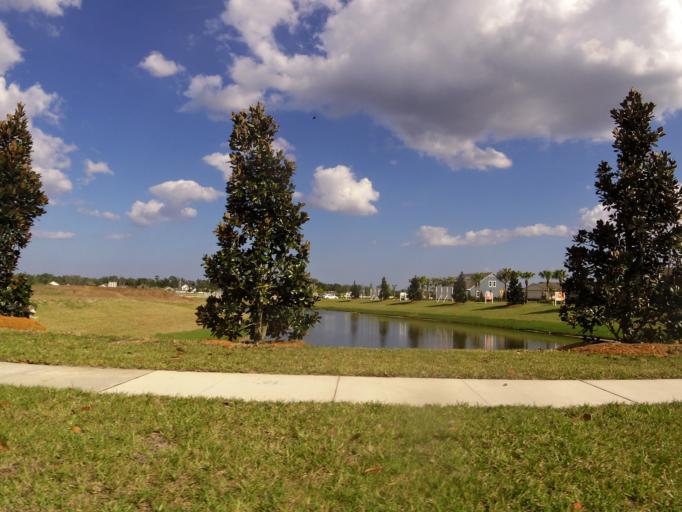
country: US
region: Florida
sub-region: Saint Johns County
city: Palm Valley
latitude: 30.1746
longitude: -81.5098
